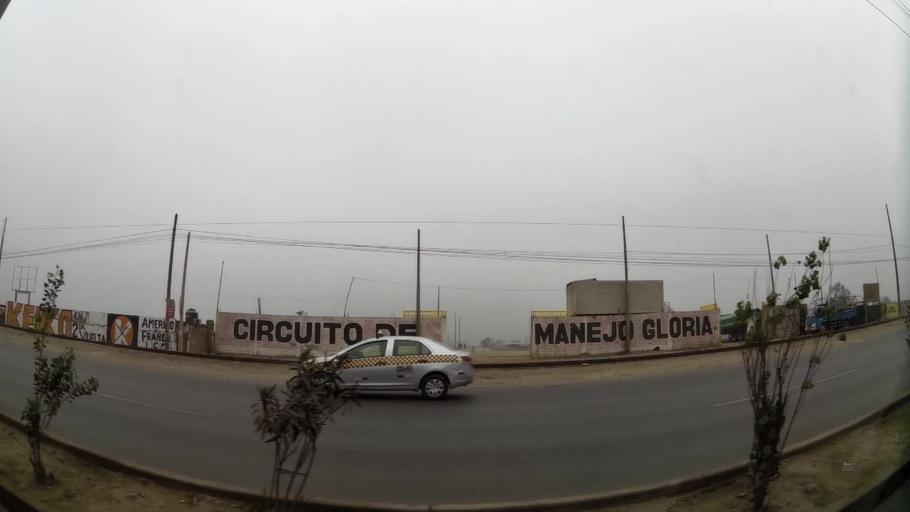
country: PE
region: Lima
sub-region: Lima
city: Santa Maria
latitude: -12.0078
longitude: -76.8579
